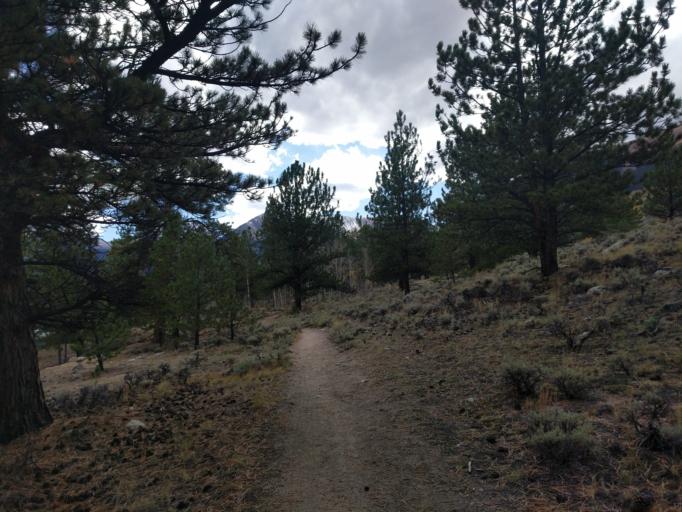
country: US
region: Colorado
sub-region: Lake County
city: Leadville
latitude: 39.0977
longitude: -106.3699
